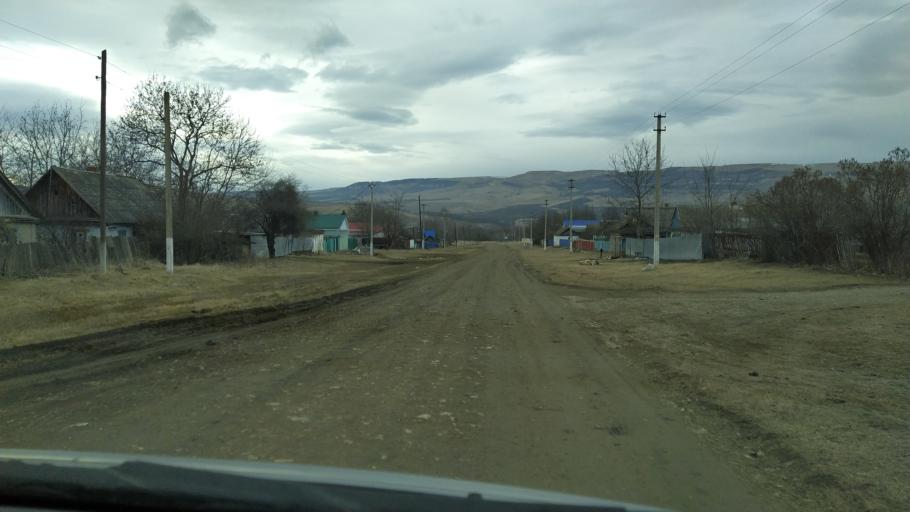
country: RU
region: Krasnodarskiy
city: Peredovaya
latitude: 44.0830
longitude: 41.3678
